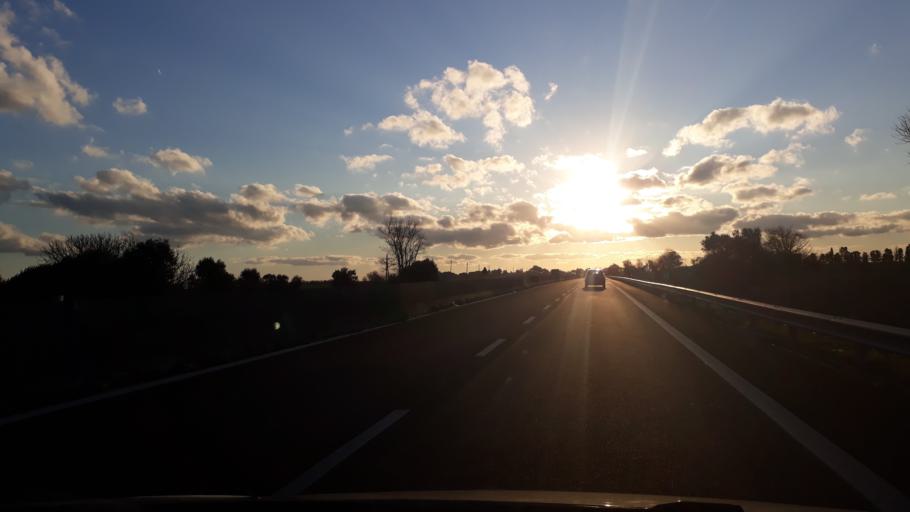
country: IT
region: Apulia
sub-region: Provincia di Brindisi
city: Brindisi
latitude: 40.6765
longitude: 17.8465
